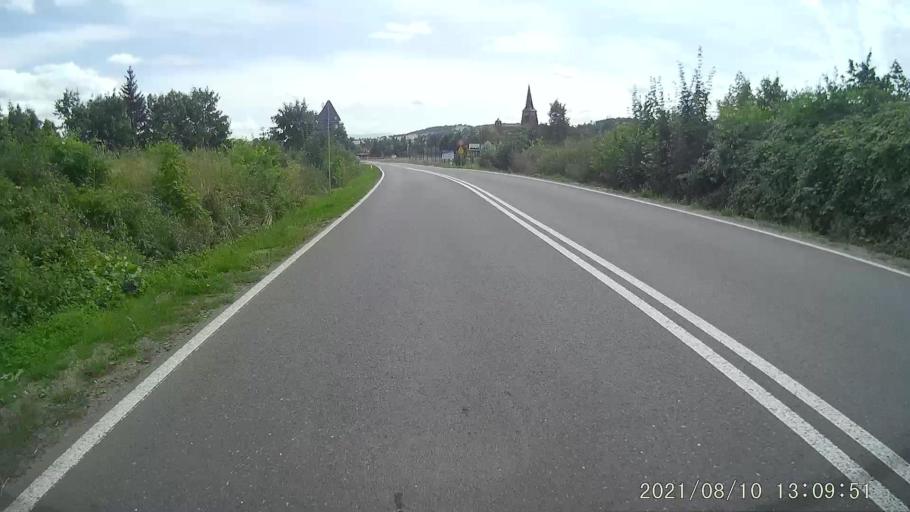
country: PL
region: Lower Silesian Voivodeship
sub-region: Powiat klodzki
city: Bozkow
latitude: 50.4991
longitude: 16.5361
